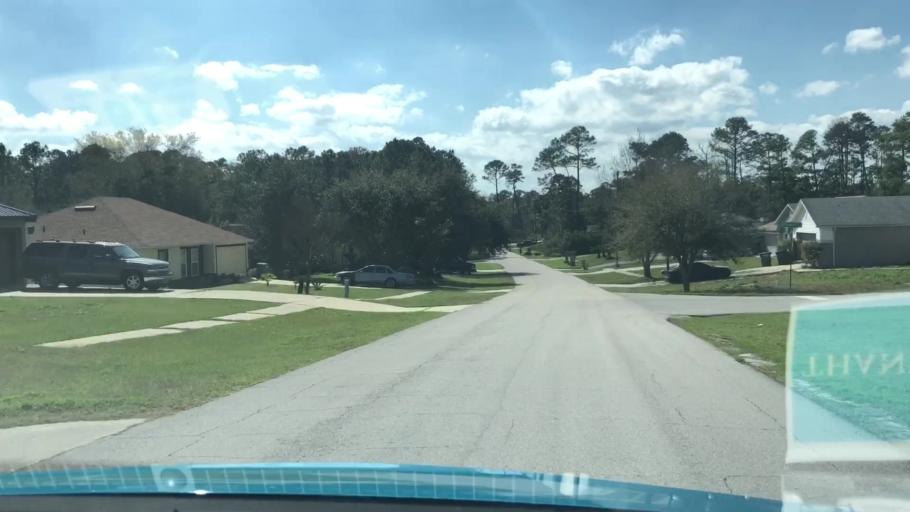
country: US
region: Florida
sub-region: Volusia County
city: Lake Helen
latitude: 28.9582
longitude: -81.1883
